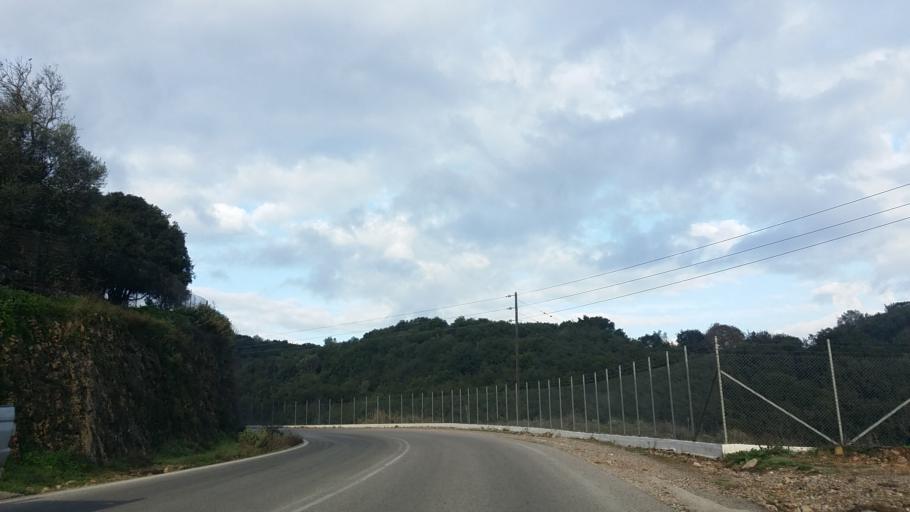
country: GR
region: West Greece
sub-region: Nomos Aitolias kai Akarnanias
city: Katouna
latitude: 38.7803
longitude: 21.1236
